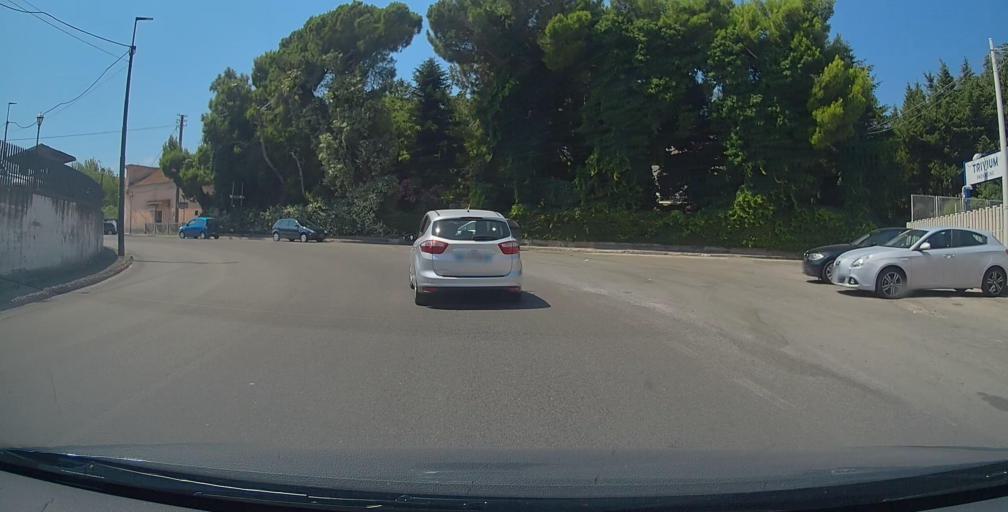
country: IT
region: Campania
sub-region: Provincia di Salerno
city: Cava De Tirreni
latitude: 40.7125
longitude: 14.7003
